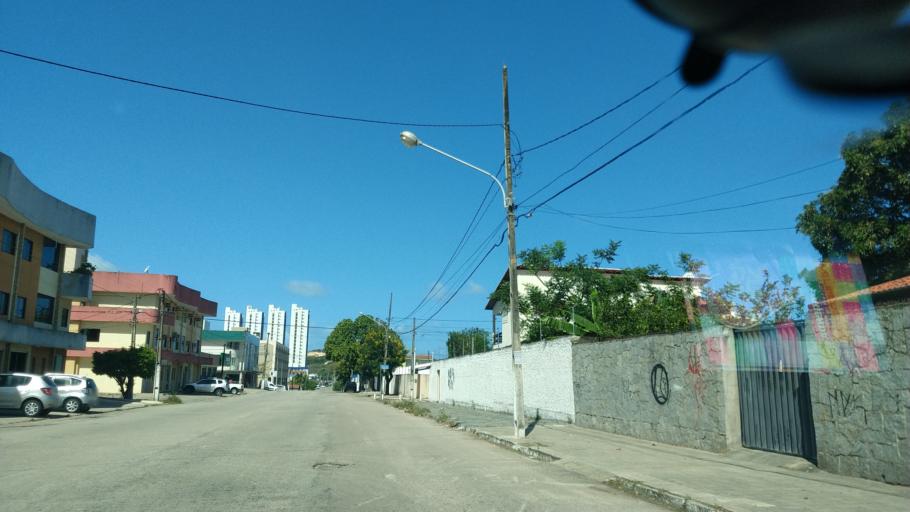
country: BR
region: Rio Grande do Norte
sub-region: Natal
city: Natal
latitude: -5.8723
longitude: -35.1894
